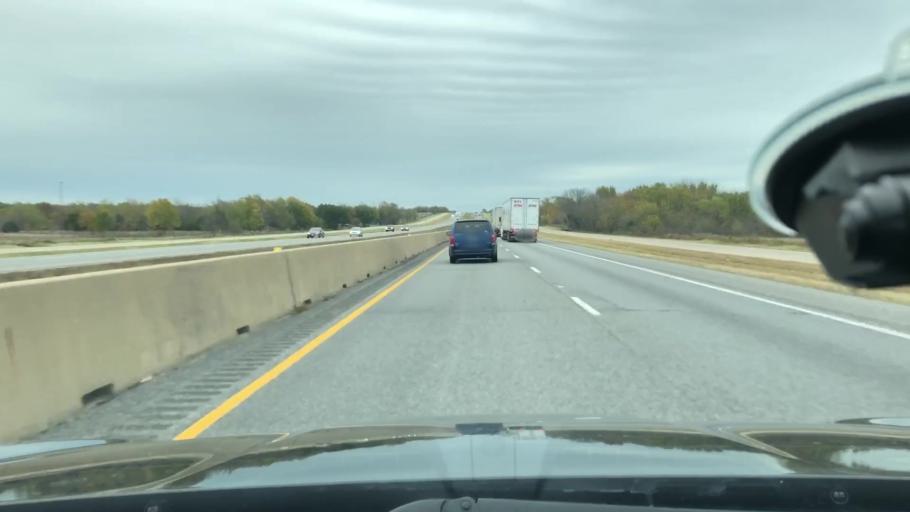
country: US
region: Texas
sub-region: Hunt County
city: Commerce
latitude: 33.1296
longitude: -95.8692
